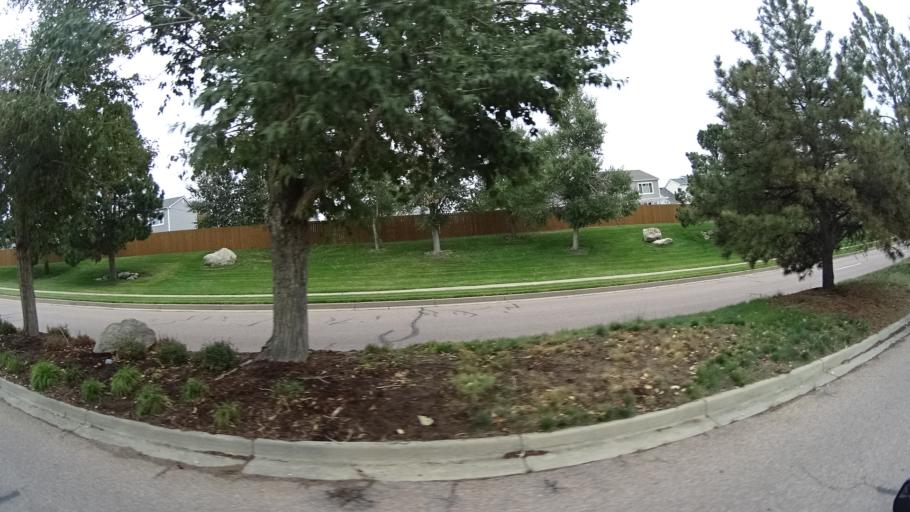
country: US
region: Colorado
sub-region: El Paso County
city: Cimarron Hills
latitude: 38.9111
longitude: -104.7114
